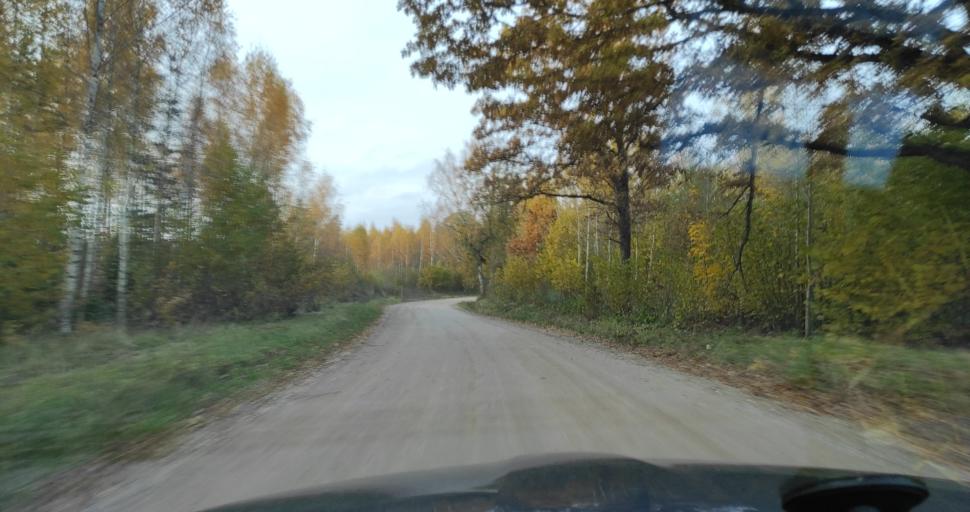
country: LV
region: Vainode
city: Vainode
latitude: 56.6276
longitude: 21.8176
